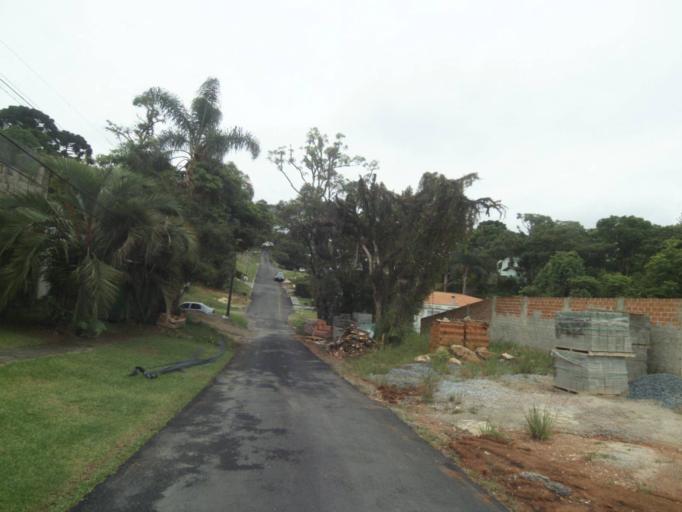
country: BR
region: Parana
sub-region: Curitiba
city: Curitiba
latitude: -25.4085
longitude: -49.2896
